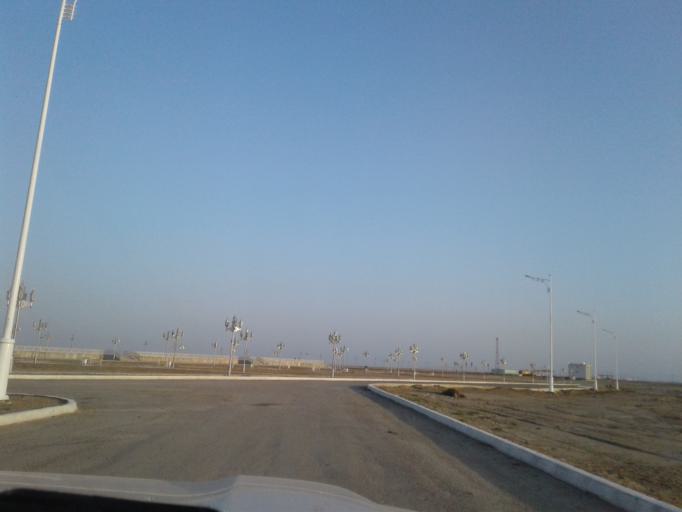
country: IR
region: Golestan
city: Aq Qayeh
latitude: 37.7056
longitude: 54.7423
